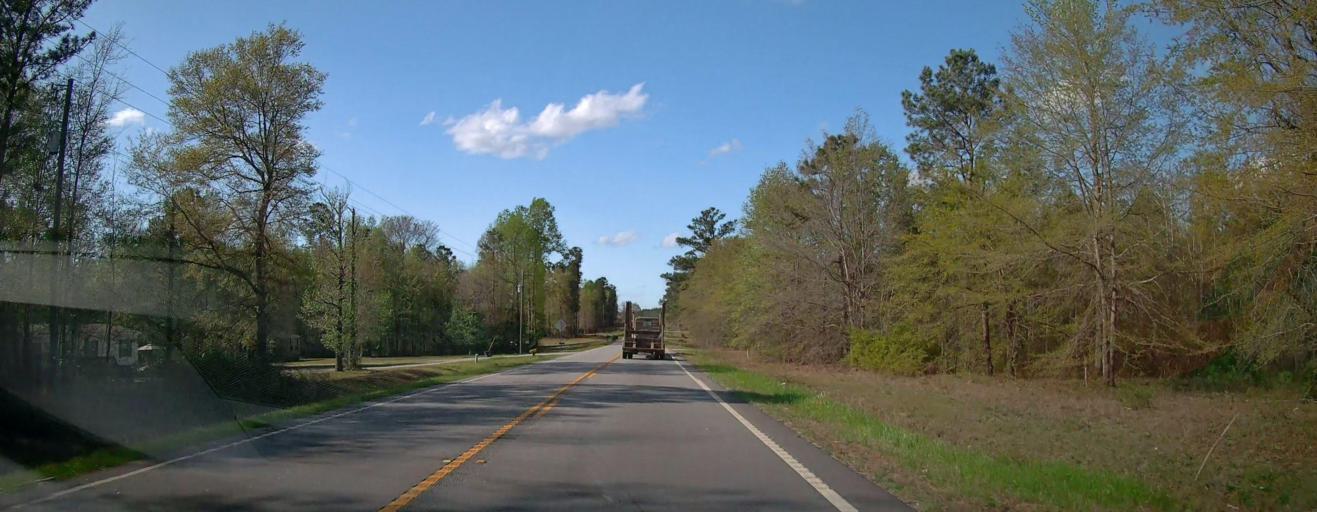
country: US
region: Georgia
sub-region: Baldwin County
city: Hardwick
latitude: 33.0669
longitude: -83.1343
